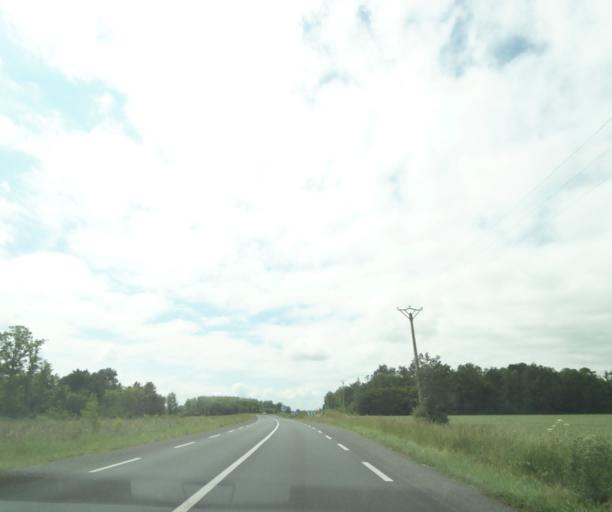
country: FR
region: Pays de la Loire
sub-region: Departement de Maine-et-Loire
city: Montreuil-Bellay
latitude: 47.0815
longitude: -0.1750
